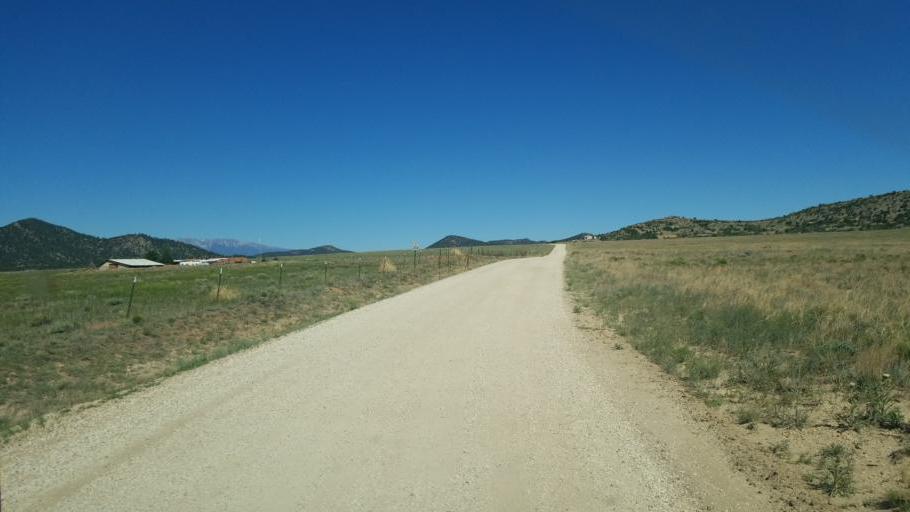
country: US
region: Colorado
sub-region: Custer County
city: Westcliffe
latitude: 38.2354
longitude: -105.4876
